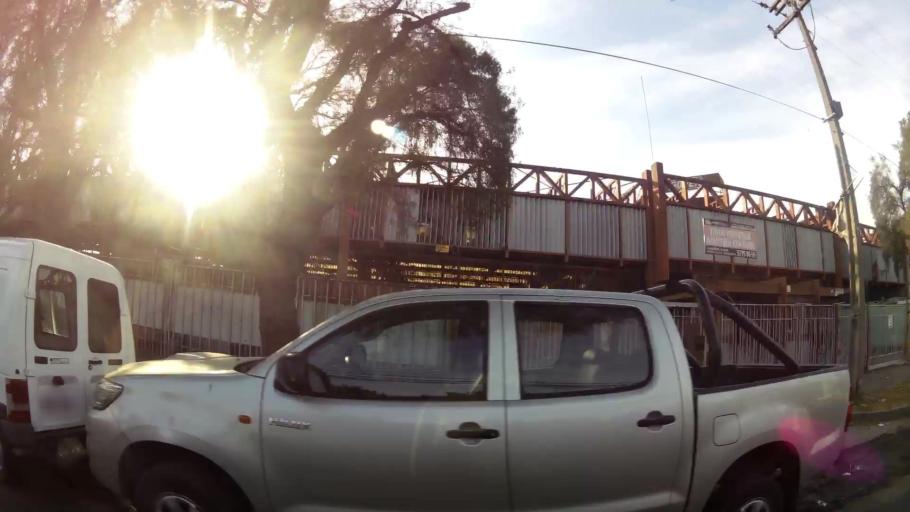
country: CL
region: Santiago Metropolitan
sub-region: Provincia de Santiago
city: Santiago
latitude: -33.5233
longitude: -70.6742
